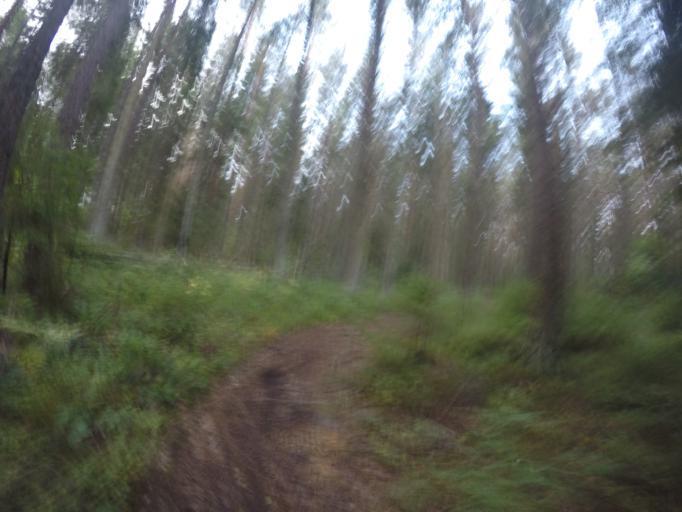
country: SE
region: Vaestmanland
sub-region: Vasteras
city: Vasteras
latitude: 59.6424
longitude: 16.5226
